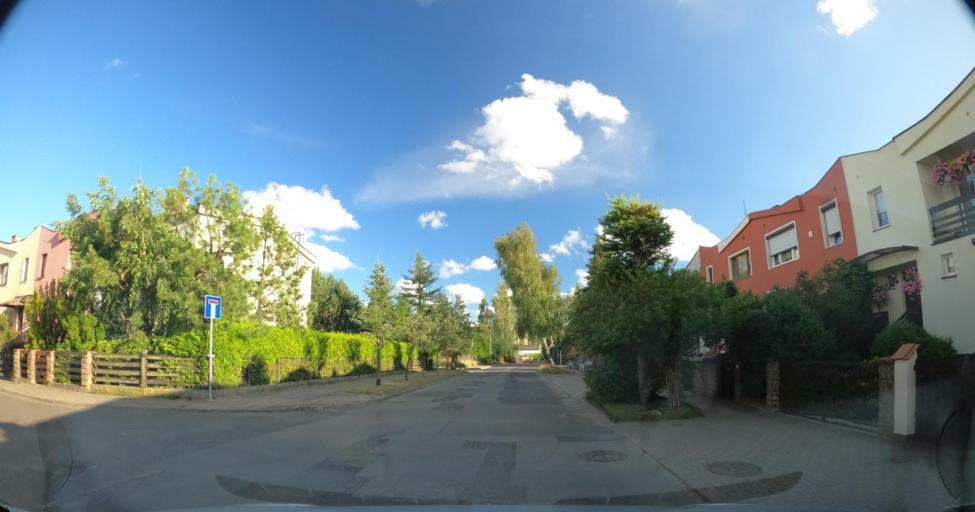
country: PL
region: Pomeranian Voivodeship
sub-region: Gdynia
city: Wielki Kack
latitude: 54.4292
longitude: 18.4742
